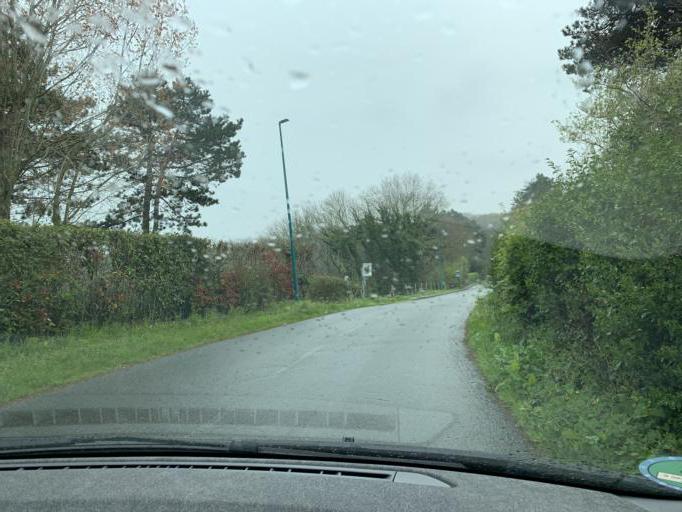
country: FR
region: Haute-Normandie
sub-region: Departement de la Seine-Maritime
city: Yport
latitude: 49.7362
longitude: 0.3087
